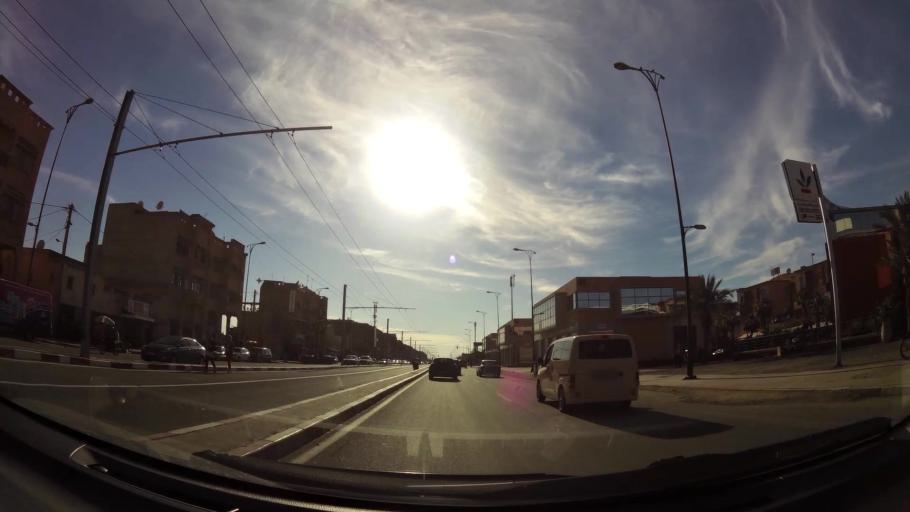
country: MA
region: Marrakech-Tensift-Al Haouz
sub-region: Marrakech
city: Marrakesh
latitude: 31.6280
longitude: -8.0609
